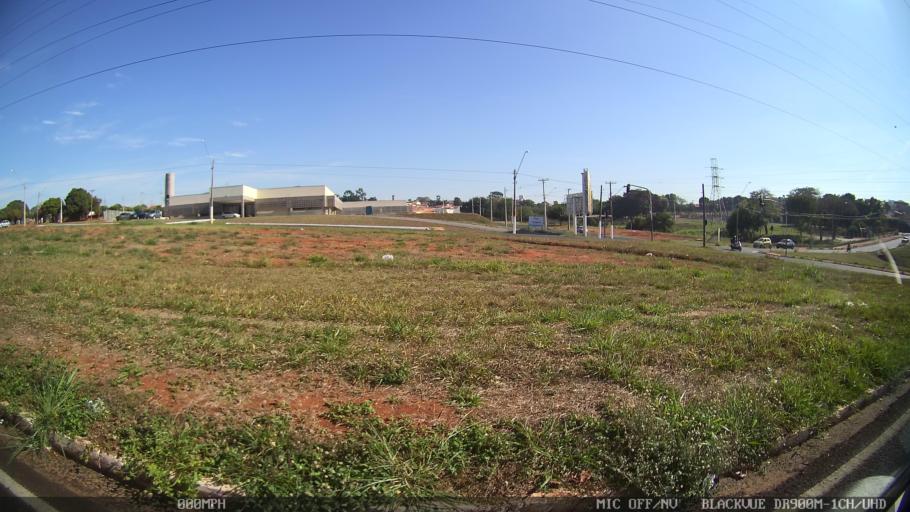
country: BR
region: Sao Paulo
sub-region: Sao Jose Do Rio Preto
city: Sao Jose do Rio Preto
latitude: -20.7902
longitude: -49.4127
